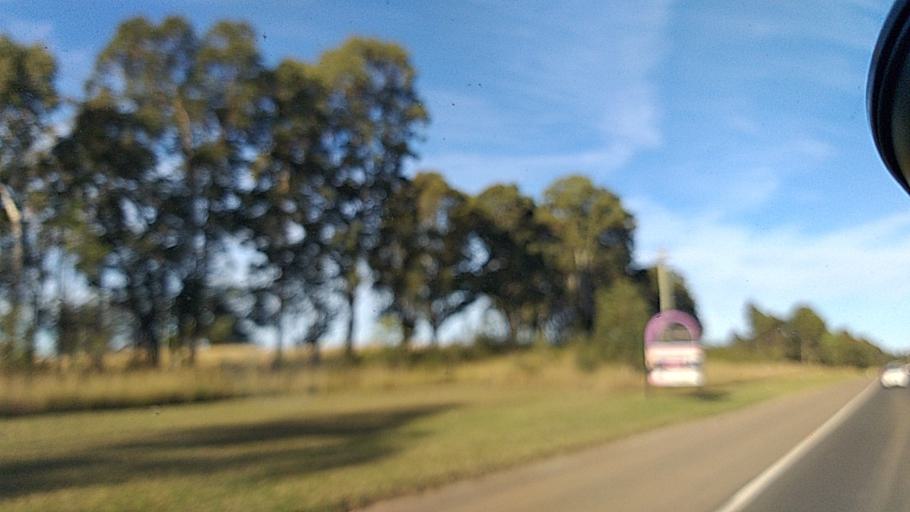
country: AU
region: New South Wales
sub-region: Blacktown
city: Riverstone
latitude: -33.6831
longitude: 150.8186
